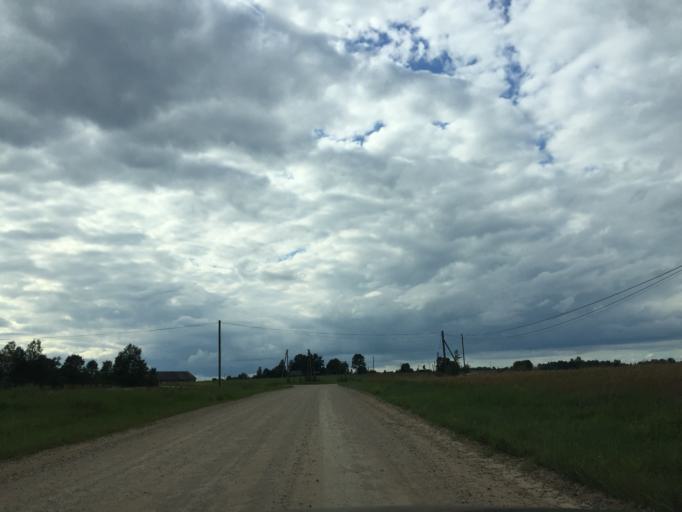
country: LV
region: Malpils
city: Malpils
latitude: 56.9653
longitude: 24.9790
